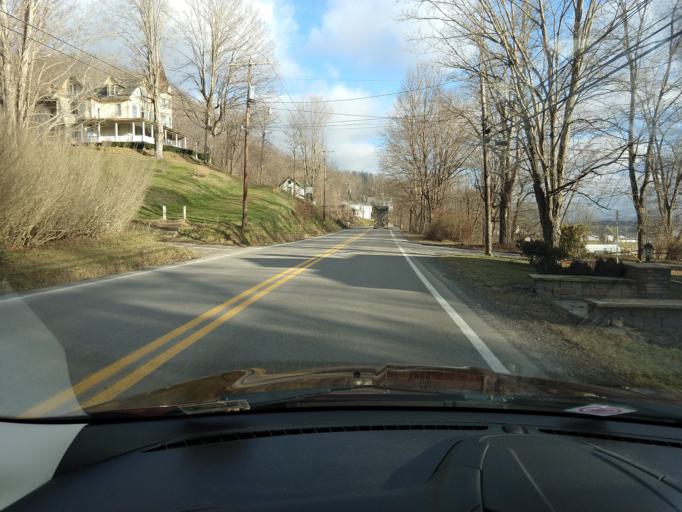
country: US
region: West Virginia
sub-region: Randolph County
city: Elkins
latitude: 38.7145
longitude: -79.9792
